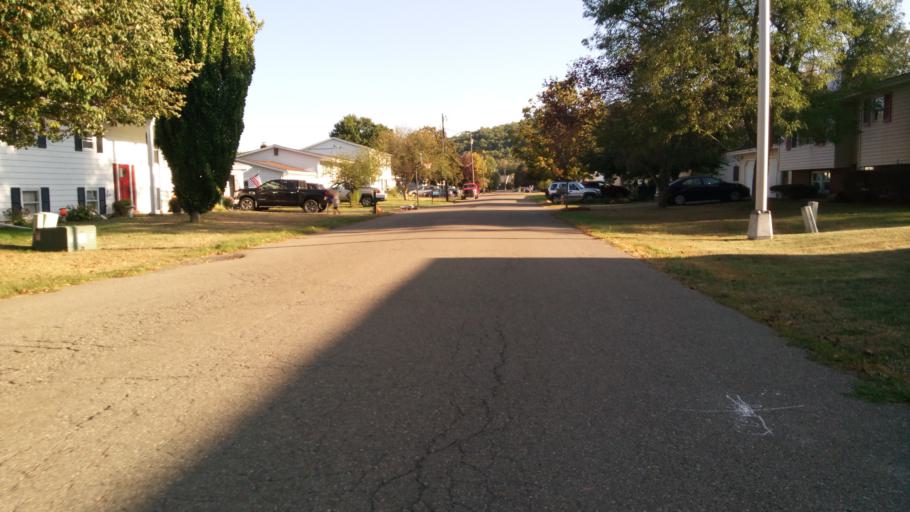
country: US
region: New York
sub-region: Chemung County
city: Southport
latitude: 42.0552
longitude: -76.8355
